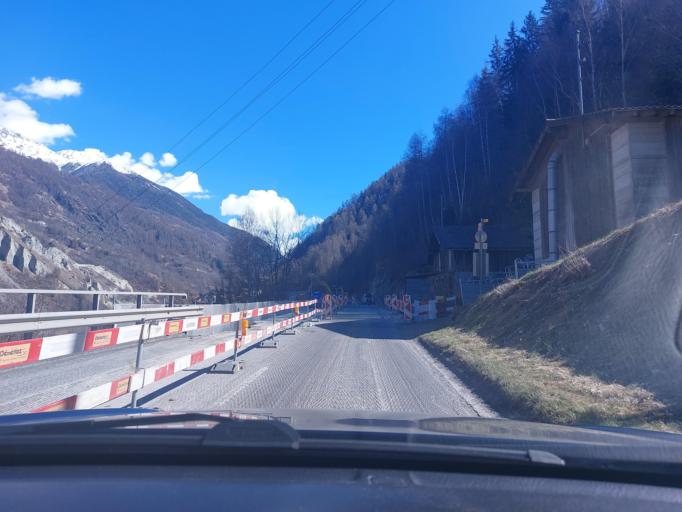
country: CH
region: Valais
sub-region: Herens District
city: Heremence
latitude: 46.1632
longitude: 7.4354
